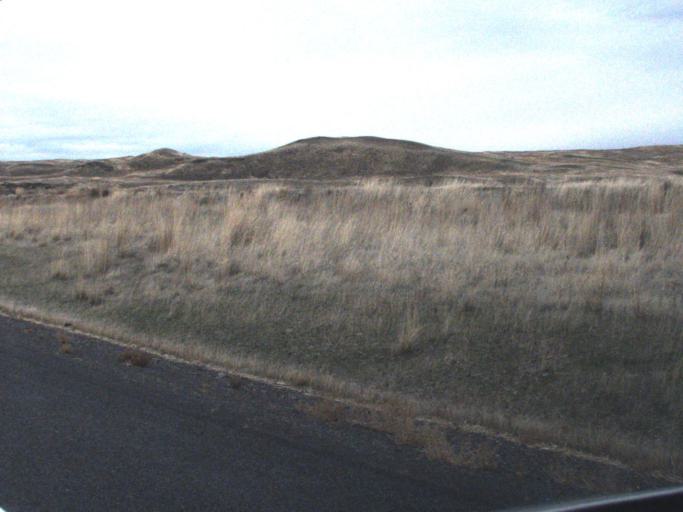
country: US
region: Washington
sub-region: Adams County
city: Ritzville
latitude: 46.7502
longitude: -118.2670
